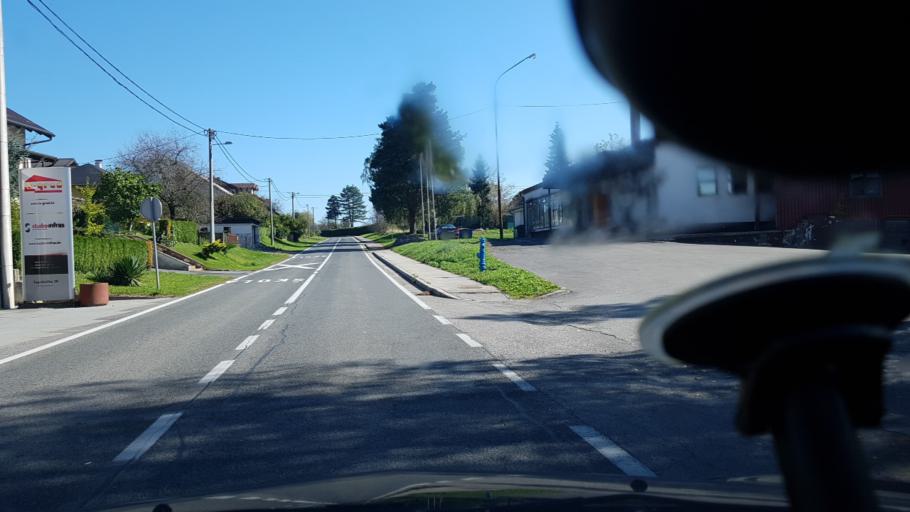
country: HR
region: Zagrebacka
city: Kriz
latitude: 45.7091
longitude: 16.4768
